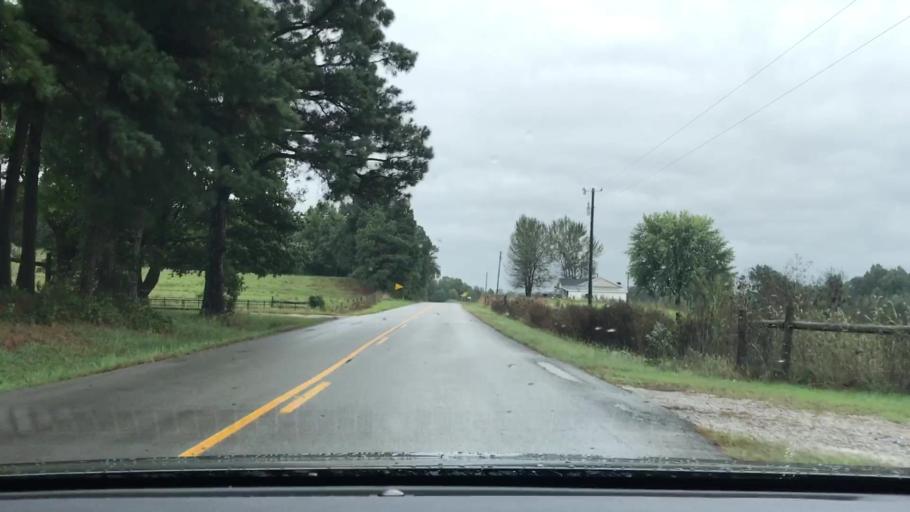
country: US
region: Kentucky
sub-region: McLean County
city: Calhoun
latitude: 37.4798
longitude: -87.2459
